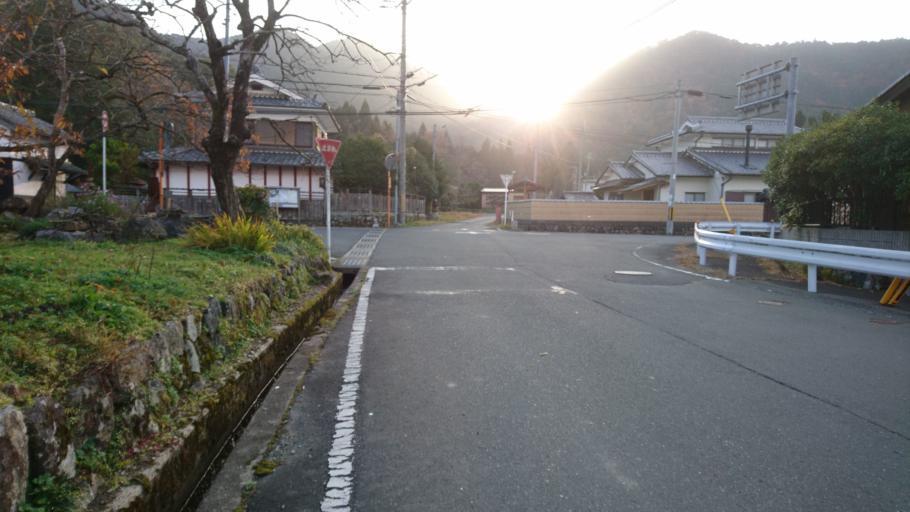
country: JP
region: Kyoto
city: Kameoka
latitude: 35.0485
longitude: 135.4703
